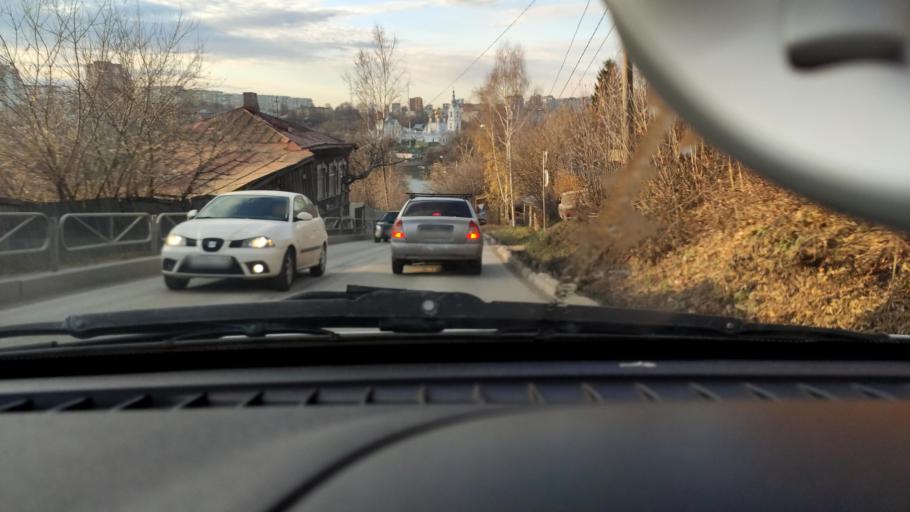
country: RU
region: Perm
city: Perm
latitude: 58.0418
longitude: 56.3267
